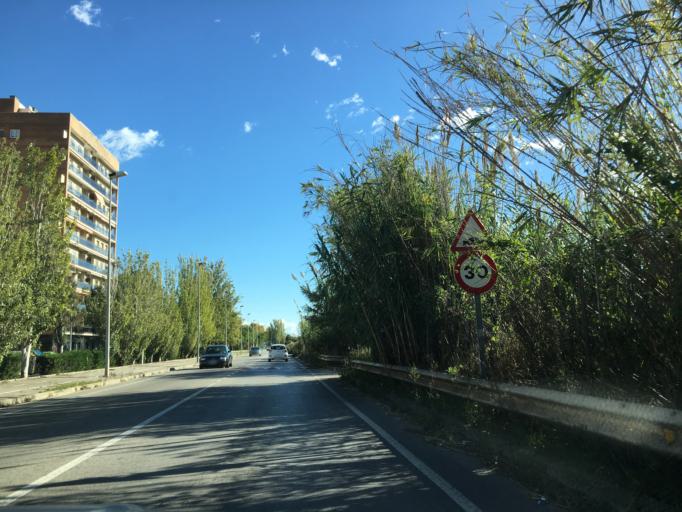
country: ES
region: Catalonia
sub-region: Provincia de Barcelona
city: Sant Joan Despi
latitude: 41.3583
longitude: 2.0595
